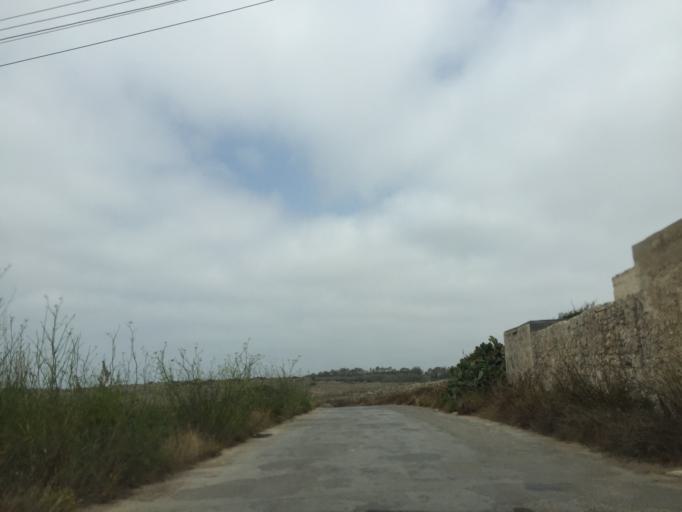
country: MT
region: Dingli
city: Dingli
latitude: 35.8807
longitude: 14.3590
